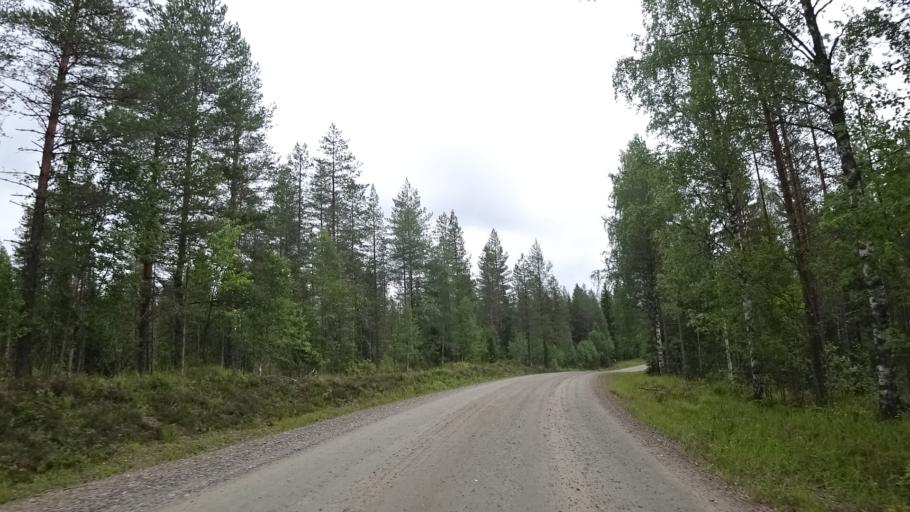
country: FI
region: North Karelia
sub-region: Joensuu
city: Ilomantsi
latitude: 63.0364
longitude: 31.2066
